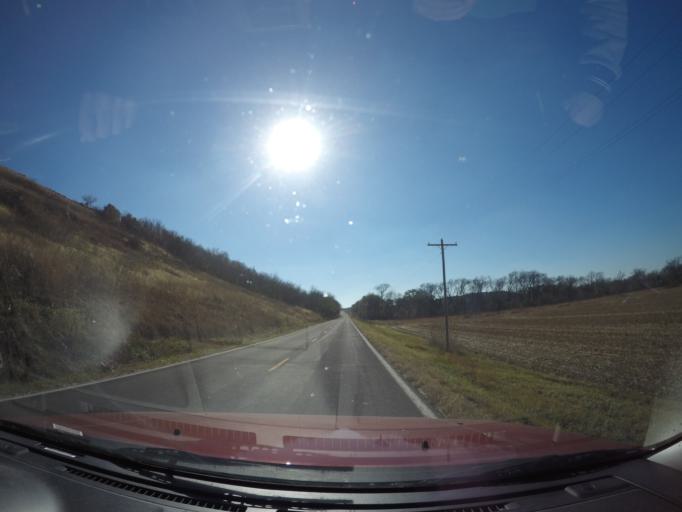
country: US
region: Kansas
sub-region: Geary County
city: Grandview Plaza
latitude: 39.0018
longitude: -96.7304
